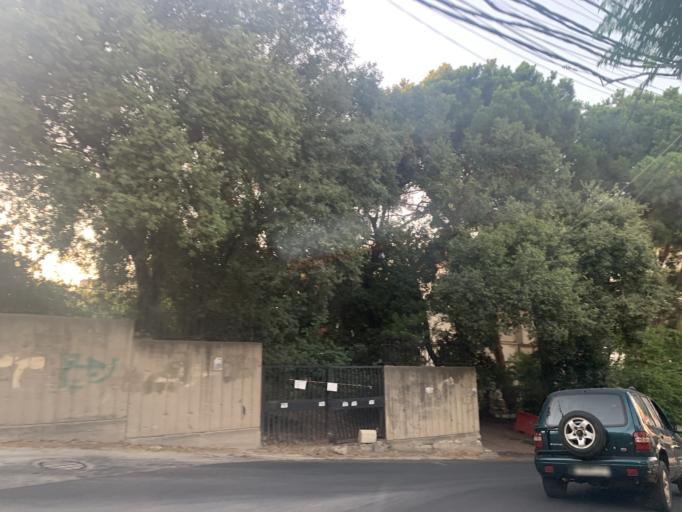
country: LB
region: Mont-Liban
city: Djounie
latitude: 33.9743
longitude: 35.6280
